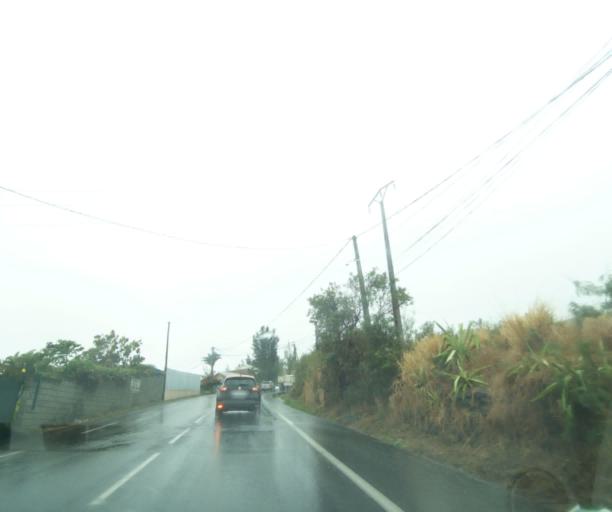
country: RE
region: Reunion
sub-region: Reunion
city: Saint-Paul
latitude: -21.0347
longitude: 55.2738
